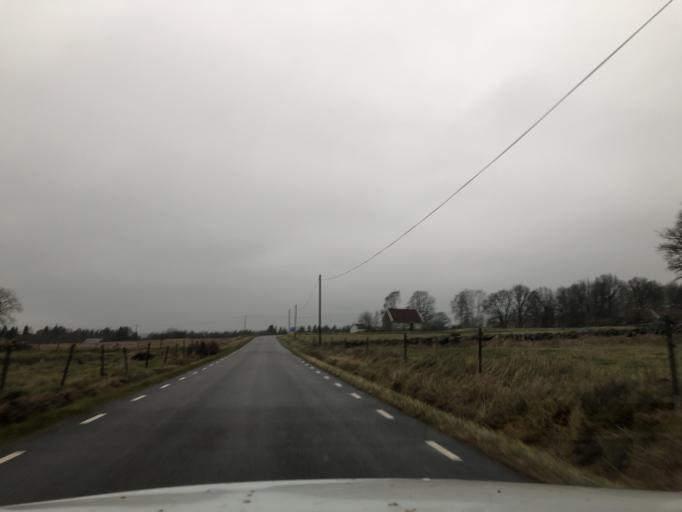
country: SE
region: Vaestra Goetaland
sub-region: Ulricehamns Kommun
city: Ulricehamn
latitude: 57.8397
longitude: 13.3786
